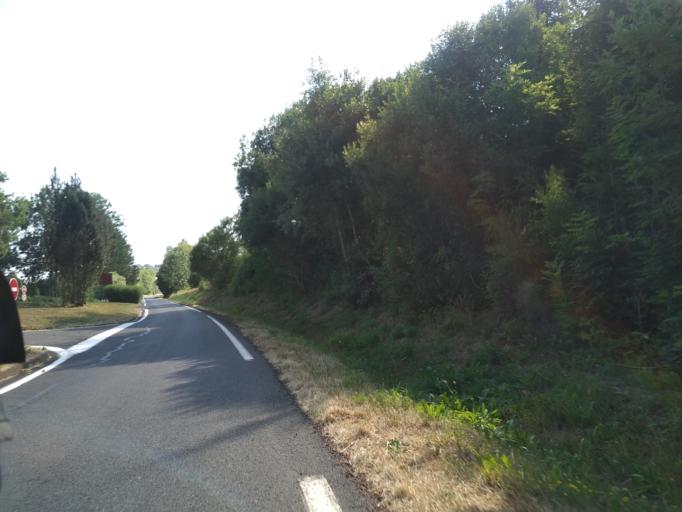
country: FR
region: Auvergne
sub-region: Departement du Cantal
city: Condat
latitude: 45.4049
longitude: 2.8233
